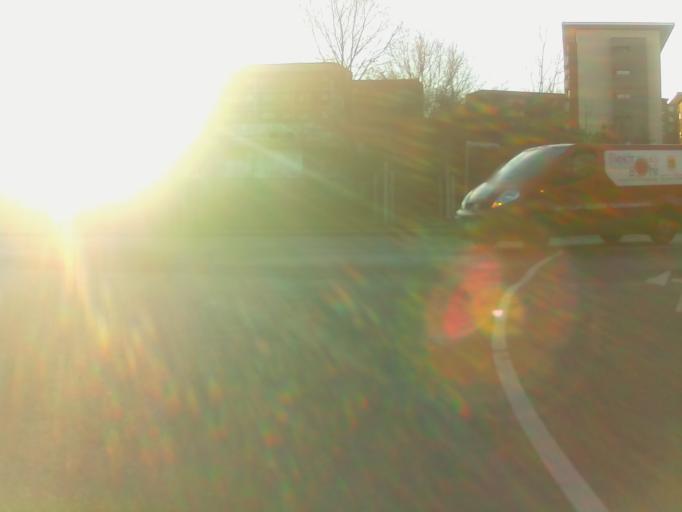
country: DE
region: Thuringia
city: Rudolstadt
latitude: 50.7005
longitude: 11.3219
